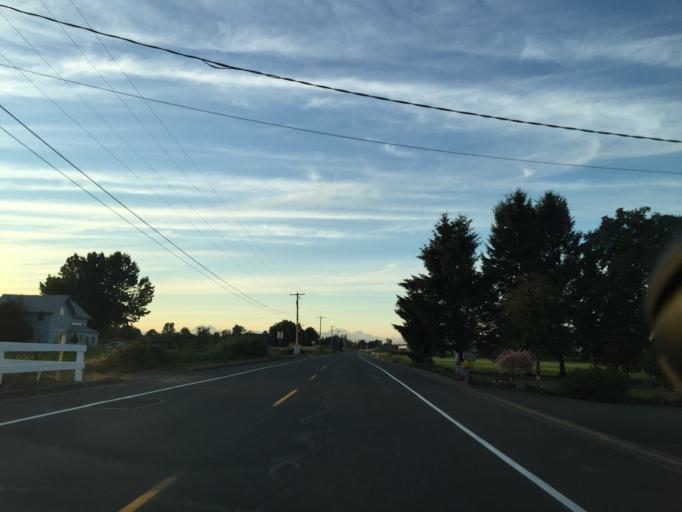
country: US
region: Washington
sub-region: Whatcom County
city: Everson
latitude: 48.9250
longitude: -122.3425
